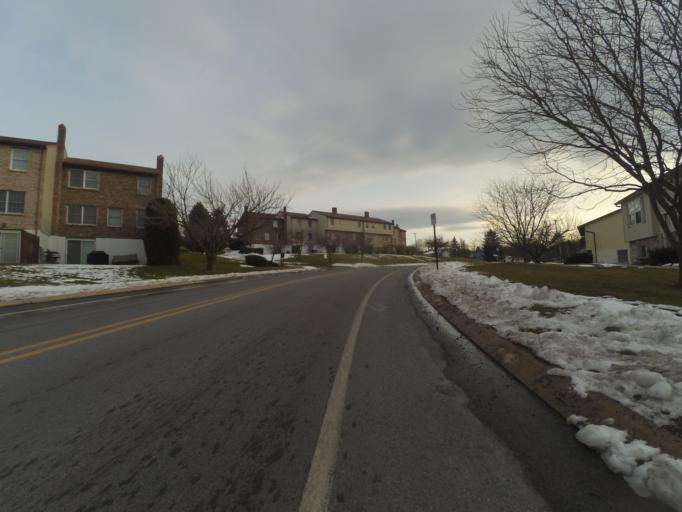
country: US
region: Pennsylvania
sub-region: Centre County
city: Houserville
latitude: 40.8315
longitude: -77.8118
